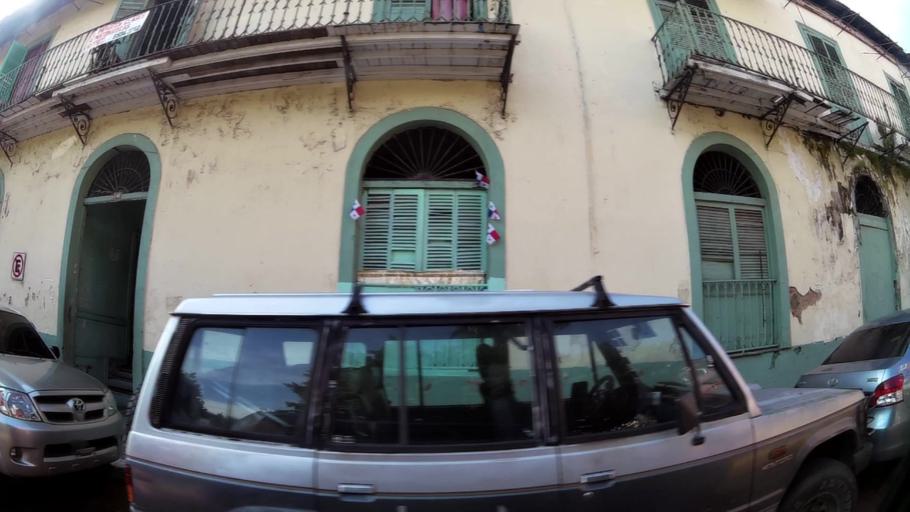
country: PA
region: Panama
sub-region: Distrito de Panama
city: Ancon
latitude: 8.9531
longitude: -79.5336
